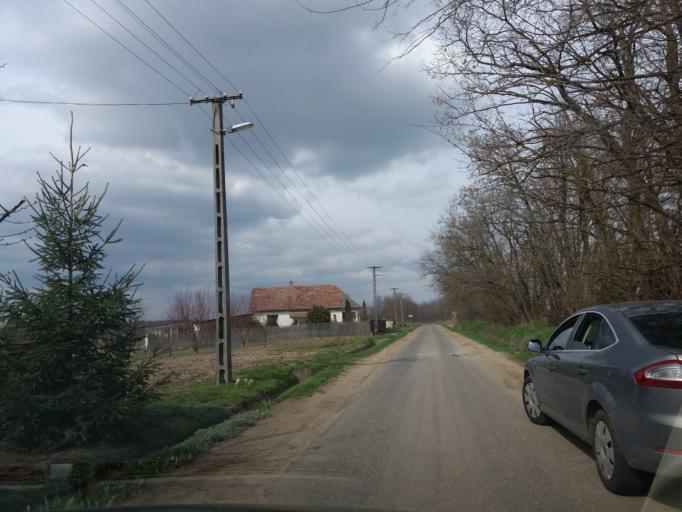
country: HU
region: Szabolcs-Szatmar-Bereg
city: Petnehaza
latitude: 48.0623
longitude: 22.0457
